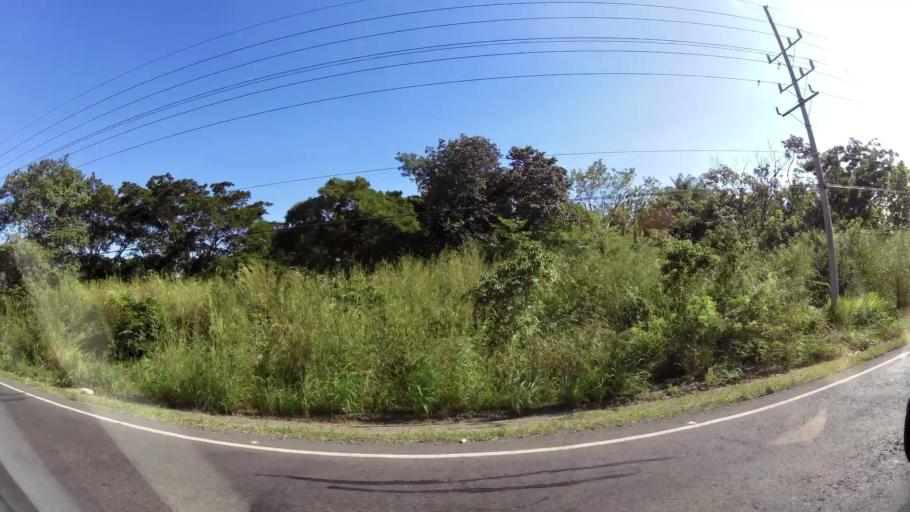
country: CR
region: Guanacaste
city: Liberia
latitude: 10.6061
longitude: -85.5082
